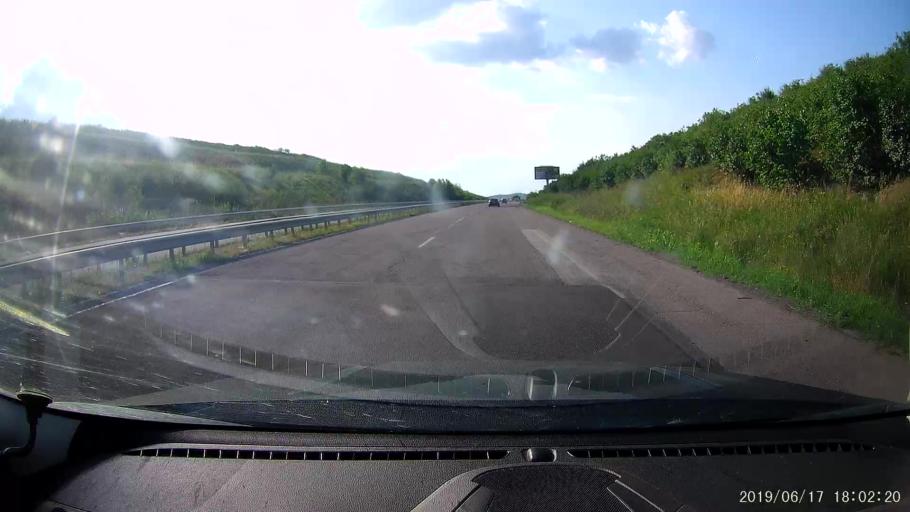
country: BG
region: Khaskovo
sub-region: Obshtina Svilengrad
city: Svilengrad
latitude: 41.7580
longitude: 26.2324
